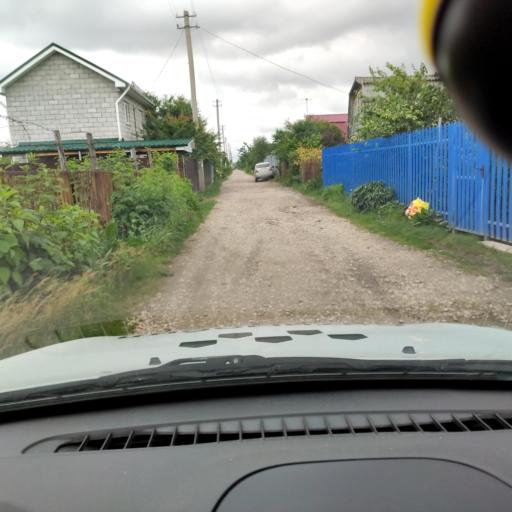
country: RU
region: Samara
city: Tol'yatti
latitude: 53.5956
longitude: 49.2908
